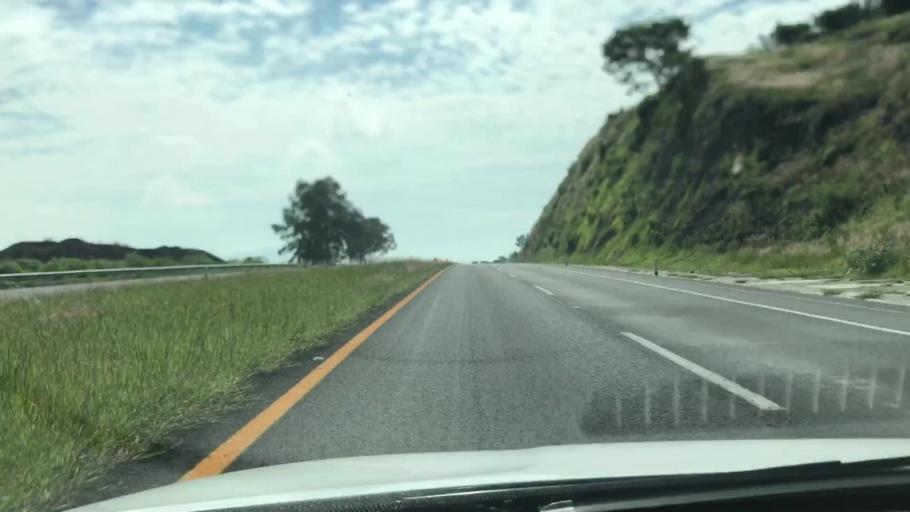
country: MX
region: Jalisco
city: Ocotlan
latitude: 20.4343
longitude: -102.7964
